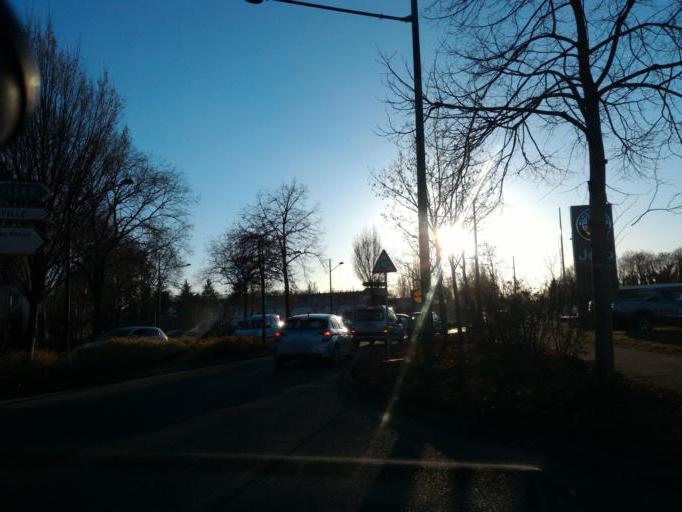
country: FR
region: Alsace
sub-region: Departement du Haut-Rhin
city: Riedisheim
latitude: 47.7625
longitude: 7.3579
